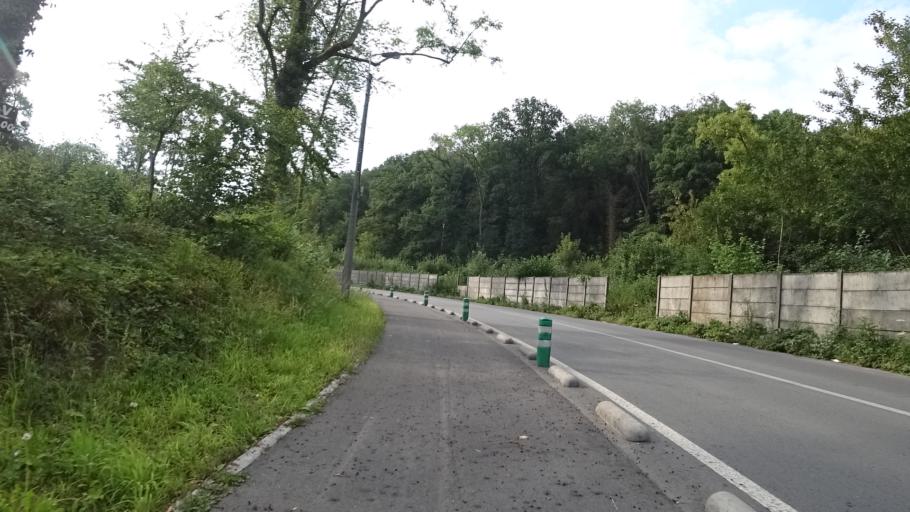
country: BE
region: Wallonia
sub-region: Province de Namur
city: Namur
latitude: 50.4864
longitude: 4.8775
